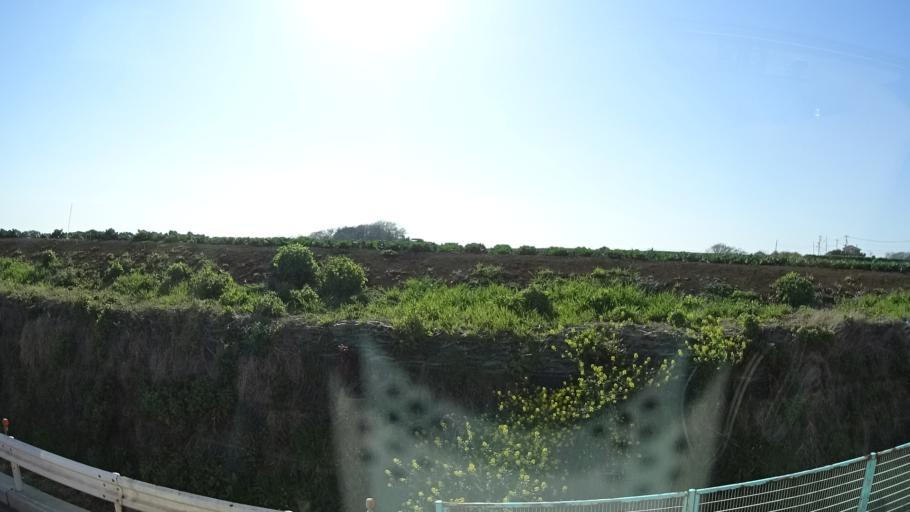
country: JP
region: Kanagawa
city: Miura
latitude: 35.1557
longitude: 139.6461
